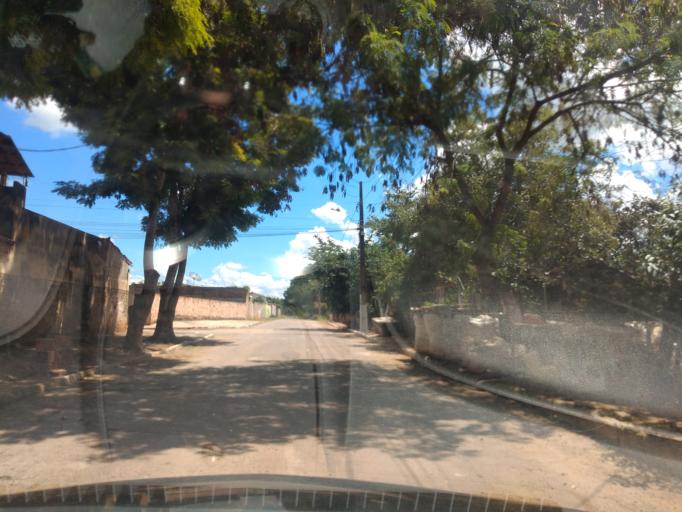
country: BR
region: Minas Gerais
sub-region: Tres Coracoes
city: Tres Coracoes
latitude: -21.6779
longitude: -45.2456
